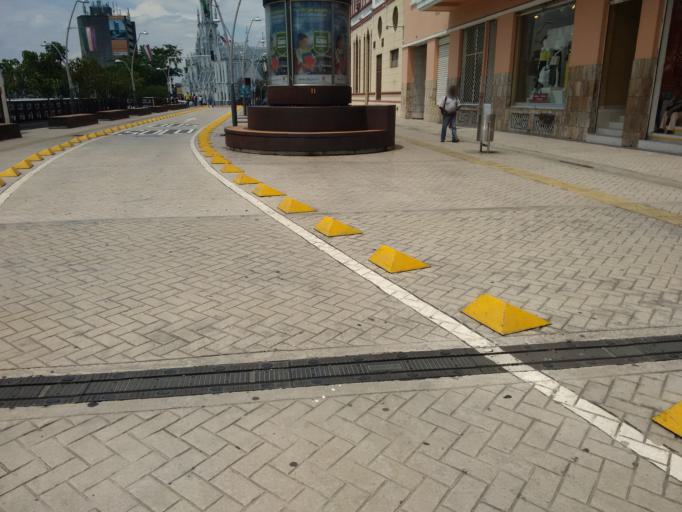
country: CO
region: Valle del Cauca
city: Cali
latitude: 3.4533
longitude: -76.5333
